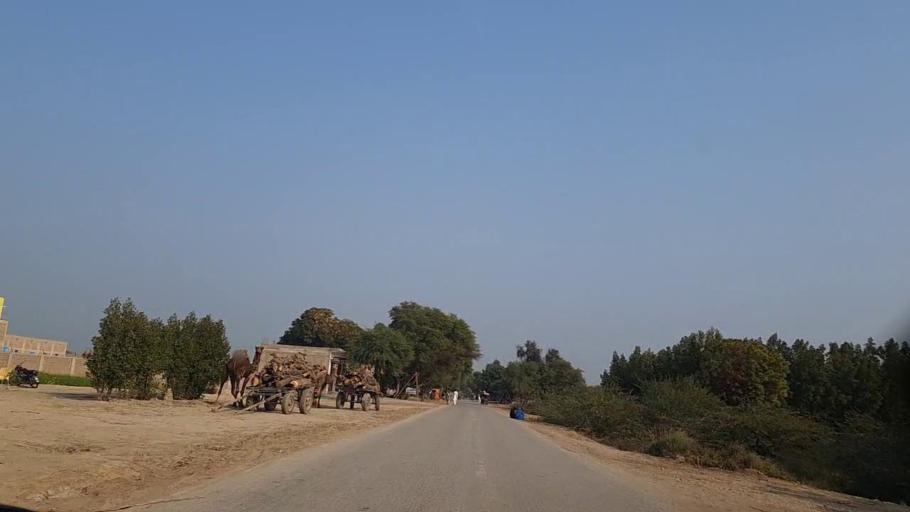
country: PK
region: Sindh
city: Sakrand
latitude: 26.1322
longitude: 68.2161
